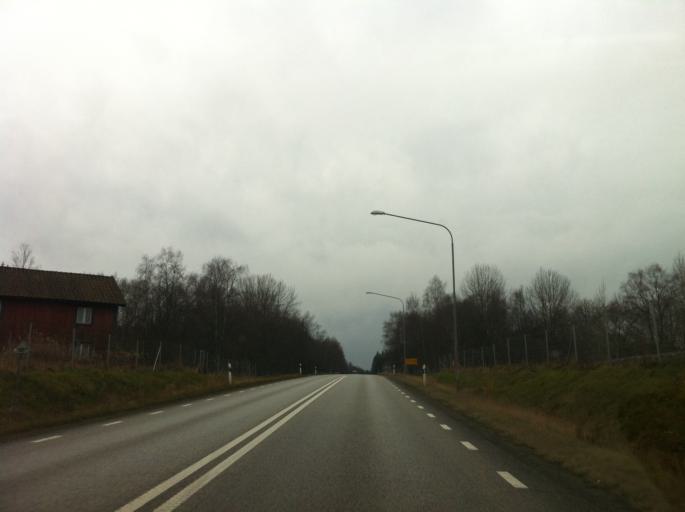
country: SE
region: Joenkoeping
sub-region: Savsjo Kommun
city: Saevsjoe
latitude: 57.3955
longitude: 14.6800
